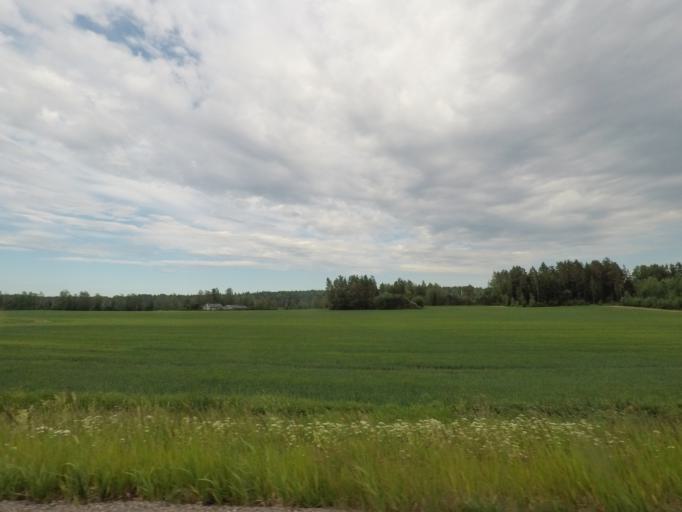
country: FI
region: Uusimaa
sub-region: Helsinki
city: Maentsaelae
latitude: 60.7524
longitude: 25.4323
